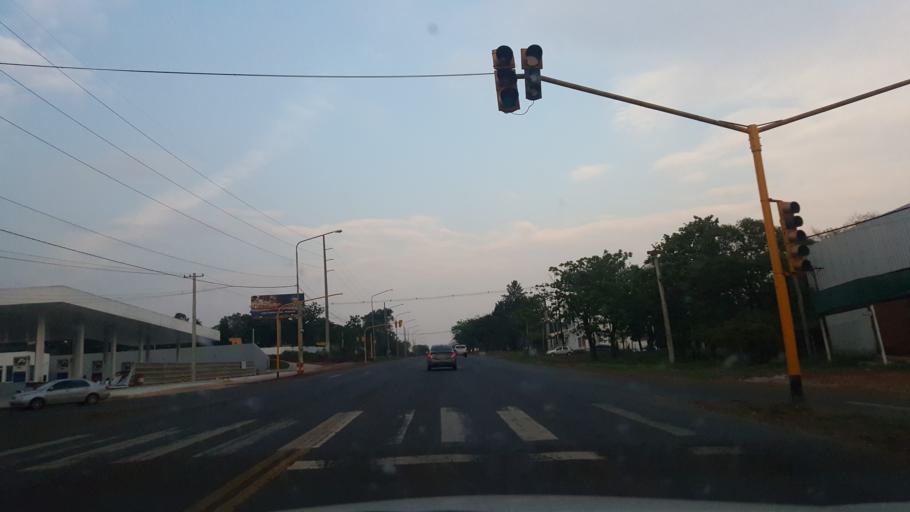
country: AR
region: Misiones
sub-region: Departamento de Capital
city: Posadas
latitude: -27.3999
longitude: -55.9443
